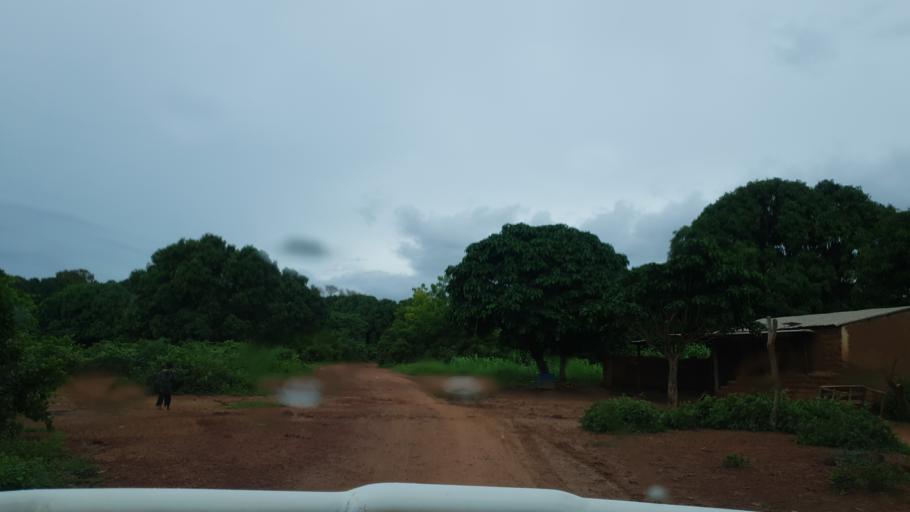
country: ML
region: Sikasso
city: Sikasso
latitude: 11.6747
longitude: -6.1722
